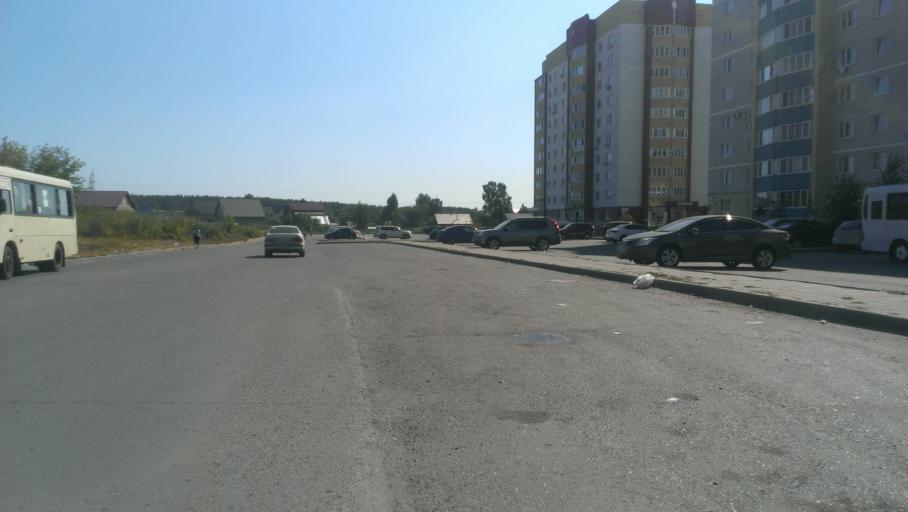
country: RU
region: Altai Krai
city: Novosilikatnyy
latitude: 53.3260
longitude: 83.6831
